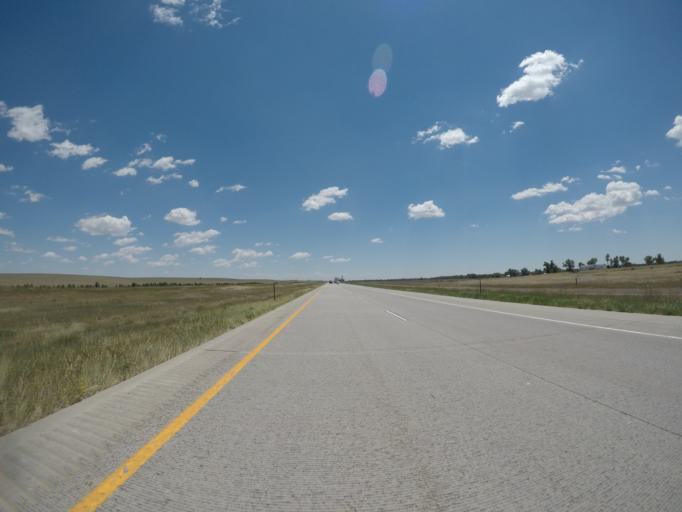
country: US
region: Colorado
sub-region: Lincoln County
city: Limon
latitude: 39.2758
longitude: -103.7473
